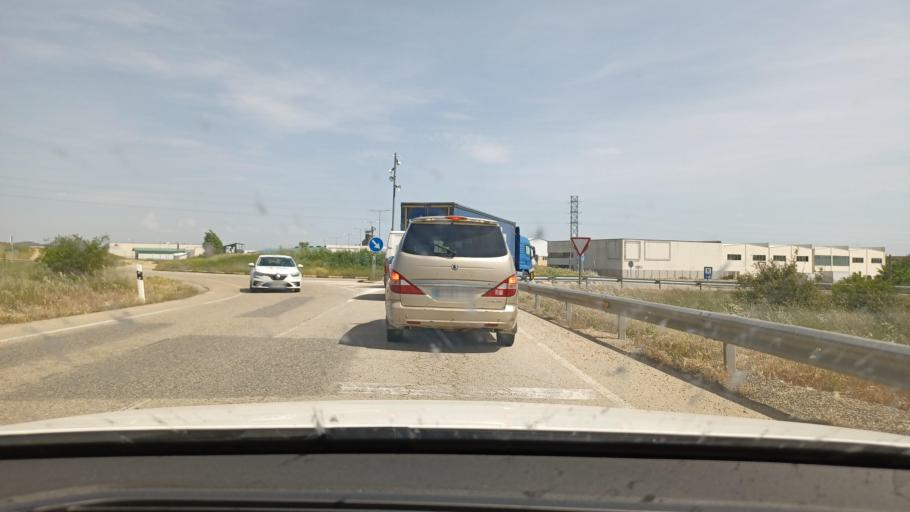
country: ES
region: Castille and Leon
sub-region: Provincia de Soria
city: Almazan
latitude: 41.4713
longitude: -2.5404
